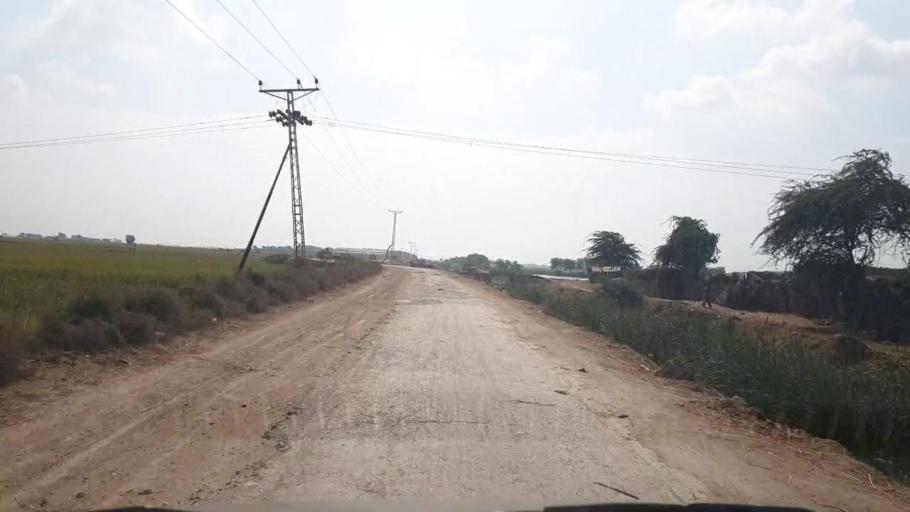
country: PK
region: Sindh
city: Kario
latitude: 24.6430
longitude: 68.5441
